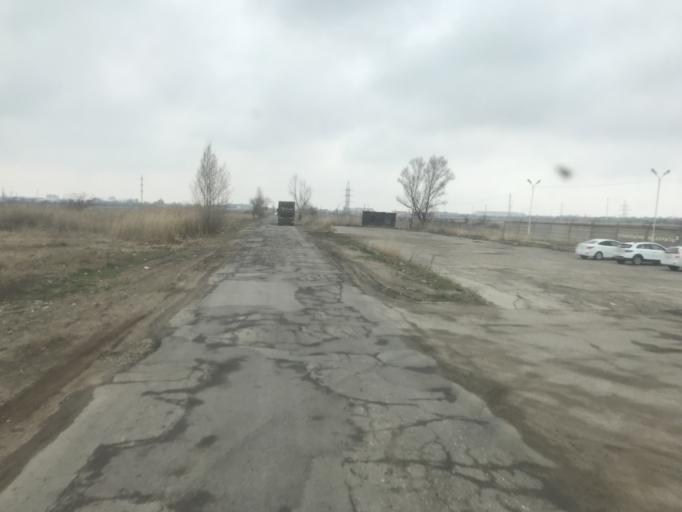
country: RU
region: Volgograd
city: Svetlyy Yar
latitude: 48.5159
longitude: 44.6309
